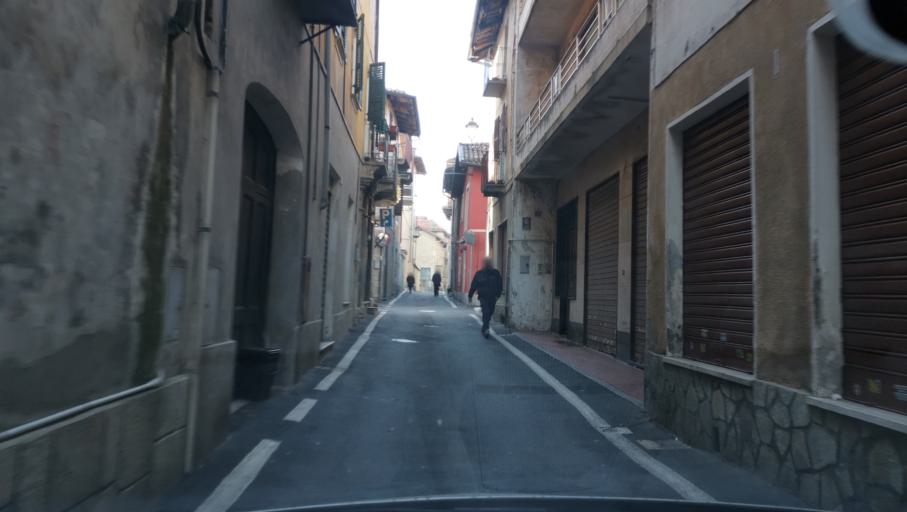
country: IT
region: Piedmont
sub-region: Provincia di Torino
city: Gassino Torinese
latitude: 45.1272
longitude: 7.8246
